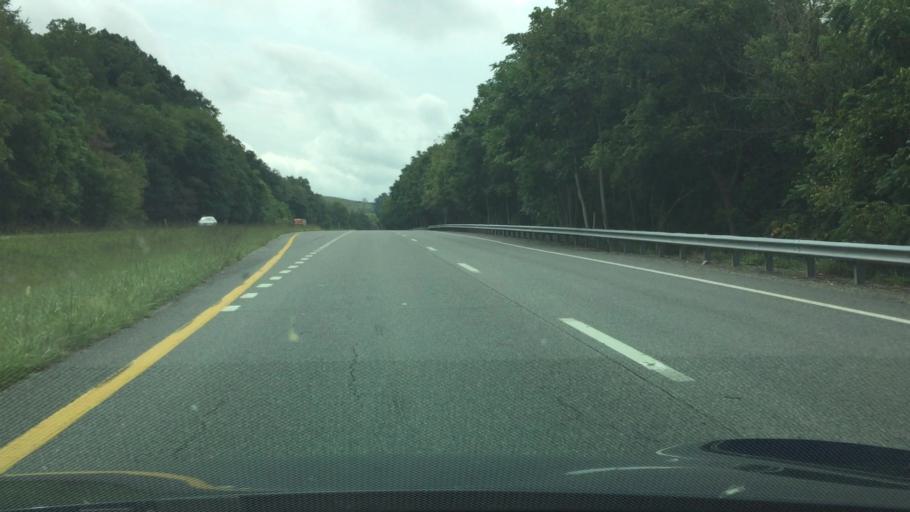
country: US
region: Virginia
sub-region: City of Radford
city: Radford
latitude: 37.1131
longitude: -80.5258
